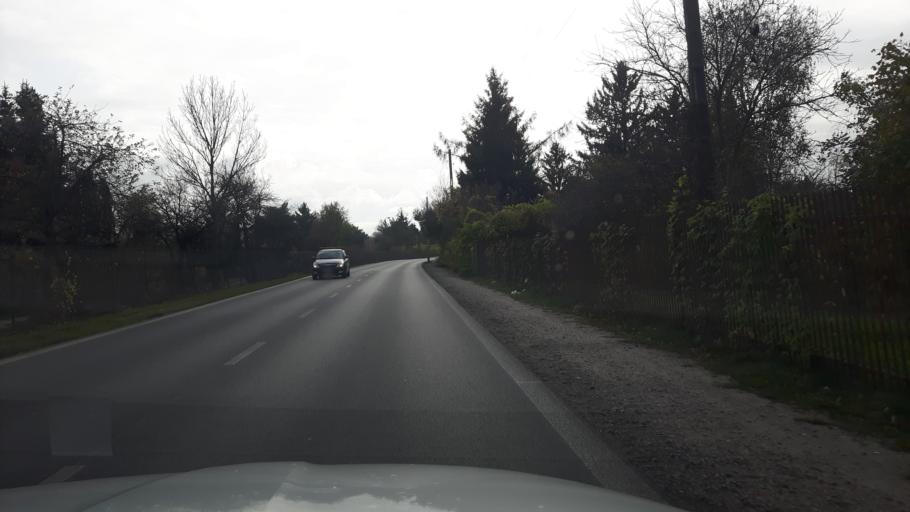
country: PL
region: Masovian Voivodeship
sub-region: Powiat wolominski
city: Zabki
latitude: 52.2818
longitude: 21.0963
